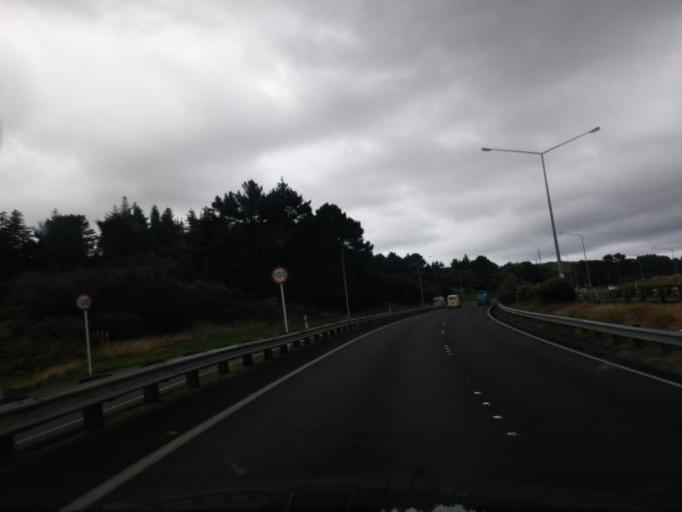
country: NZ
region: Wellington
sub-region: Porirua City
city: Porirua
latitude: -41.1855
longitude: 174.8324
